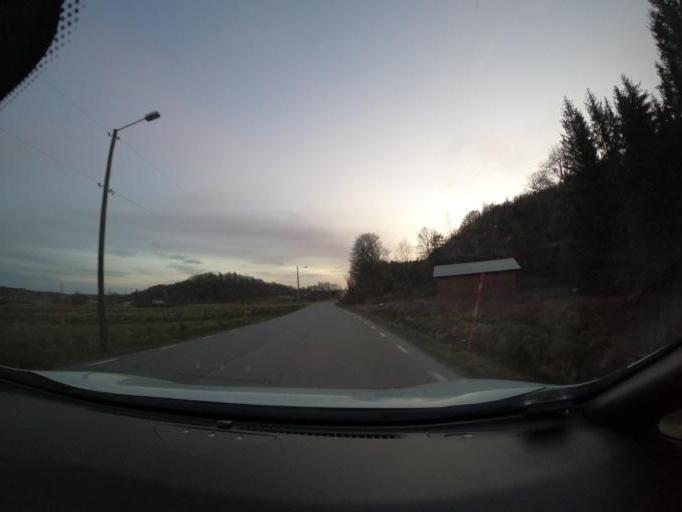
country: SE
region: Vaestra Goetaland
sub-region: Harryda Kommun
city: Molnlycke
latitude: 57.6048
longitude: 12.1368
